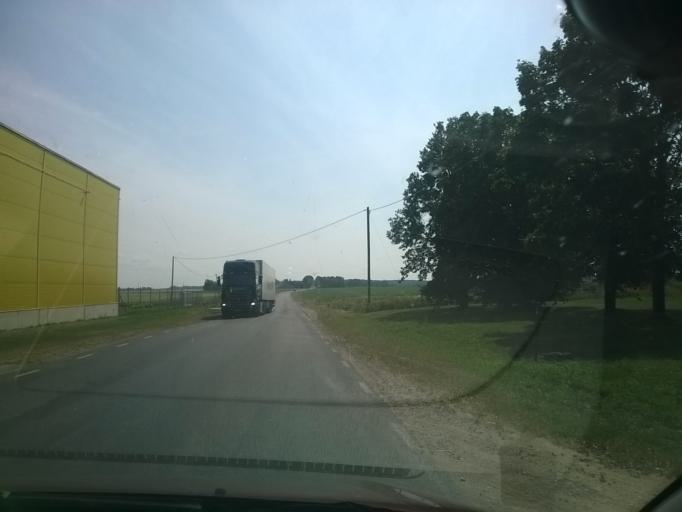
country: EE
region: Tartu
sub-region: Puhja vald
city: Puhja
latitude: 58.2807
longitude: 26.1749
